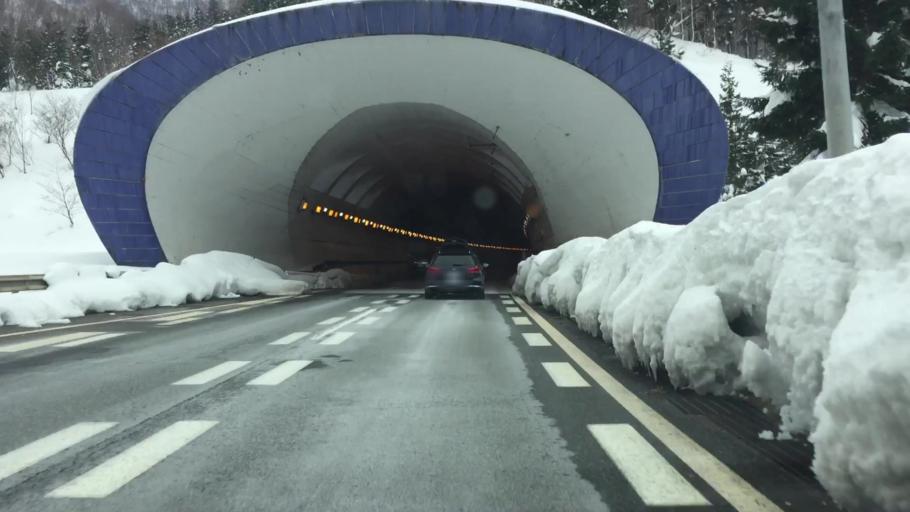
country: JP
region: Niigata
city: Shiozawa
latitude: 36.8657
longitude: 138.8757
